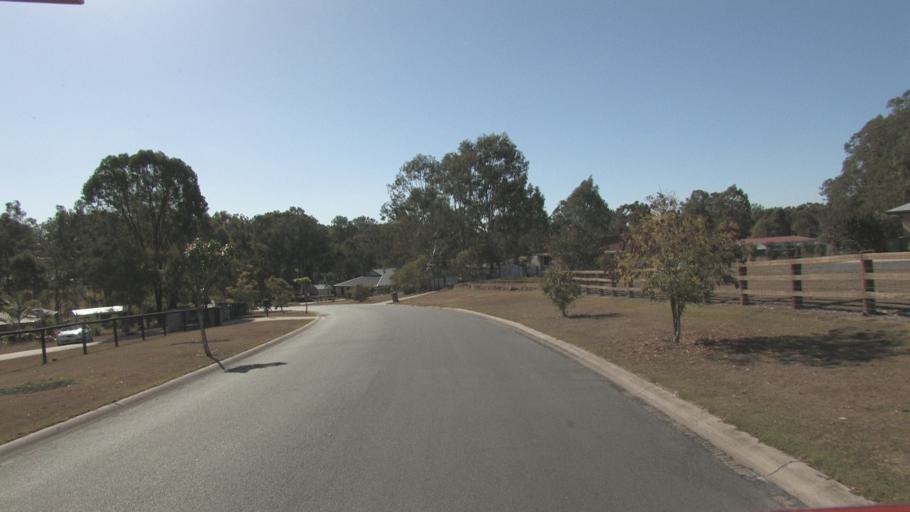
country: AU
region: Queensland
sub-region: Logan
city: Cedar Vale
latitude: -27.8628
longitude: 153.0379
